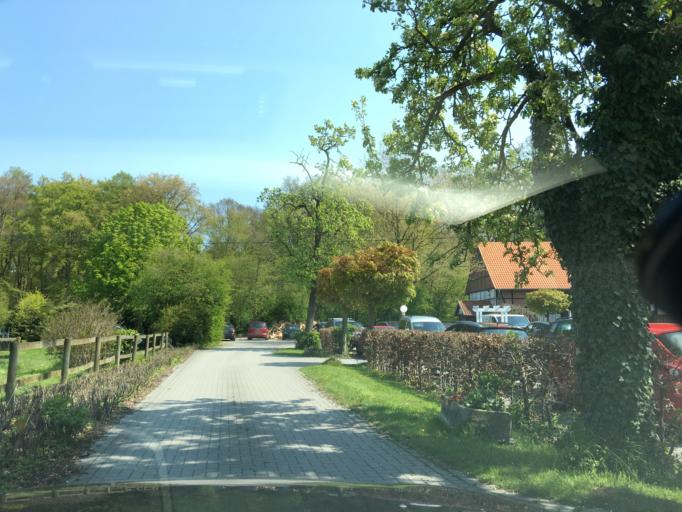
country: DE
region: North Rhine-Westphalia
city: Ludinghausen
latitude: 51.7989
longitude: 7.4344
